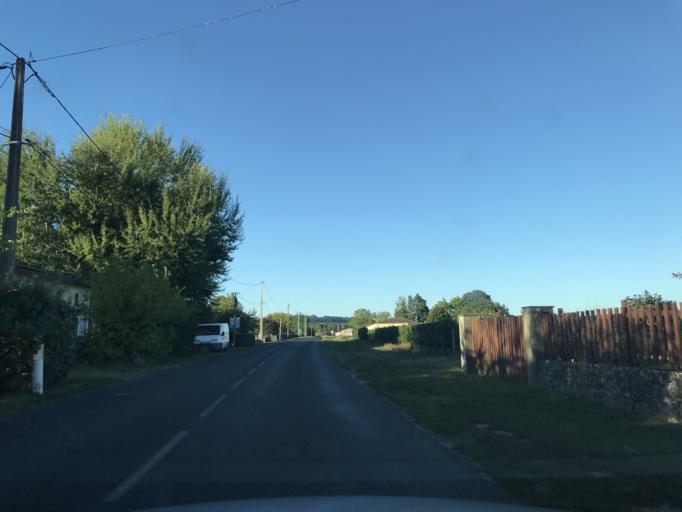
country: FR
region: Aquitaine
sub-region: Departement de la Gironde
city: Mouliets-et-Villemartin
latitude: 44.8367
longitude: -0.0389
